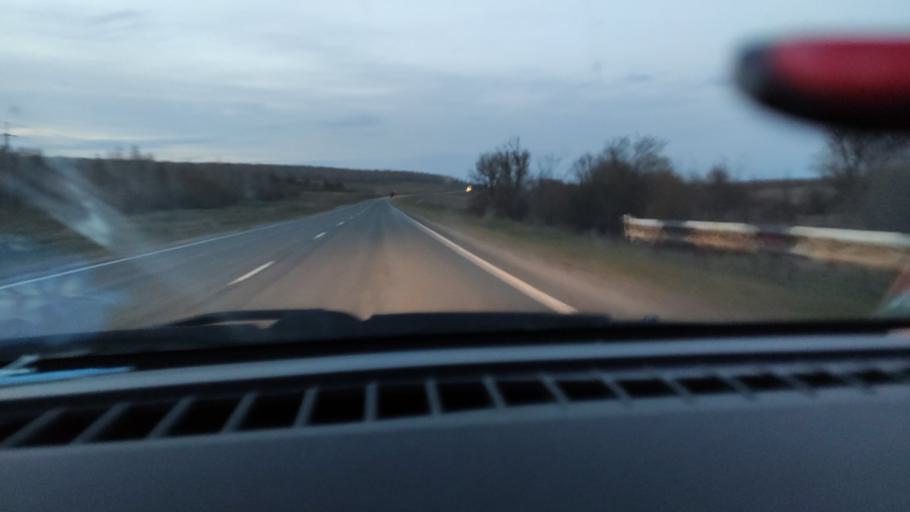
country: RU
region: Saratov
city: Sinodskoye
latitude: 52.0666
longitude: 46.7702
